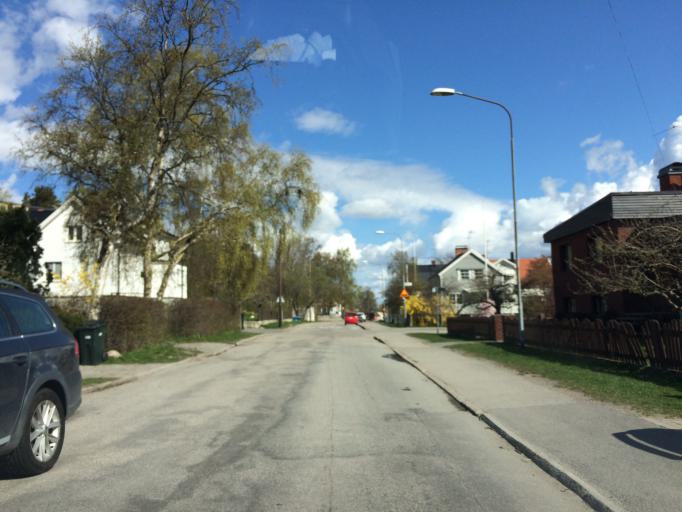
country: SE
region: Stockholm
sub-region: Huddinge Kommun
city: Segeltorp
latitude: 59.2969
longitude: 17.9483
